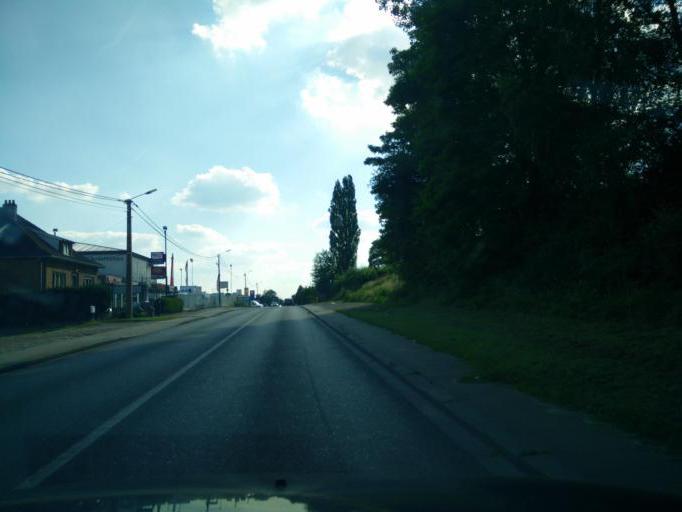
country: BE
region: Wallonia
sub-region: Province du Brabant Wallon
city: Braine-le-Chateau
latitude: 50.6896
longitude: 4.3182
